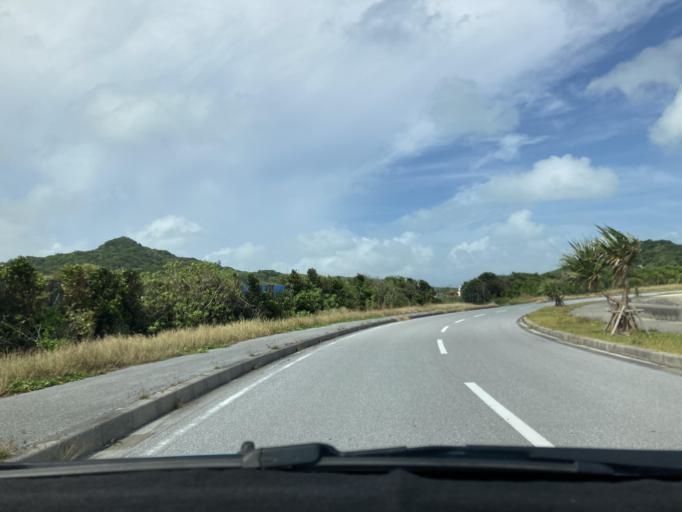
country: JP
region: Okinawa
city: Ginowan
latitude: 26.1821
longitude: 127.8212
